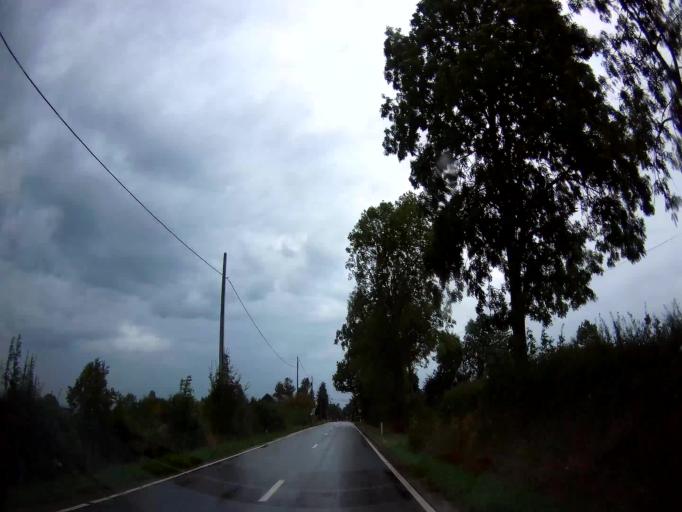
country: BE
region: Wallonia
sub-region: Province de Liege
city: Ferrieres
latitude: 50.4344
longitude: 5.6072
